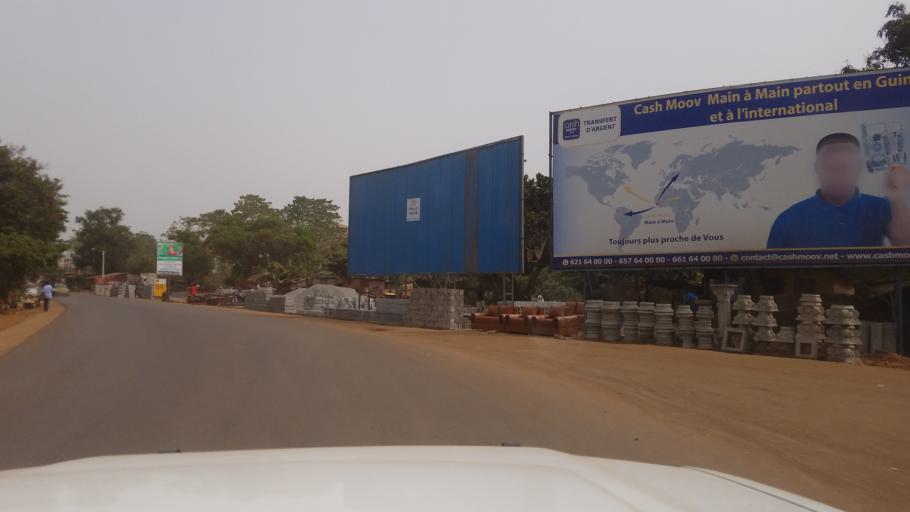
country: GN
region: Conakry
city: Conakry
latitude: 9.6475
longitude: -13.6026
